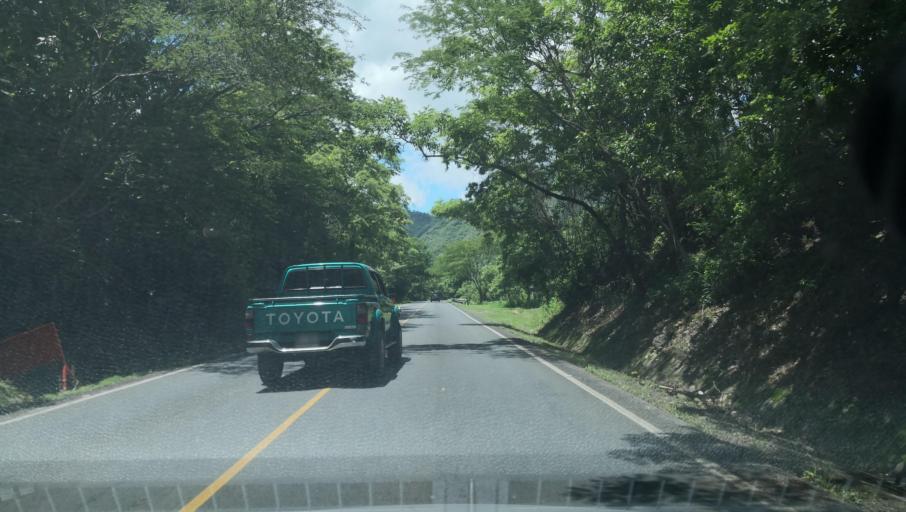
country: NI
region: Esteli
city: Condega
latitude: 13.2781
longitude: -86.3499
